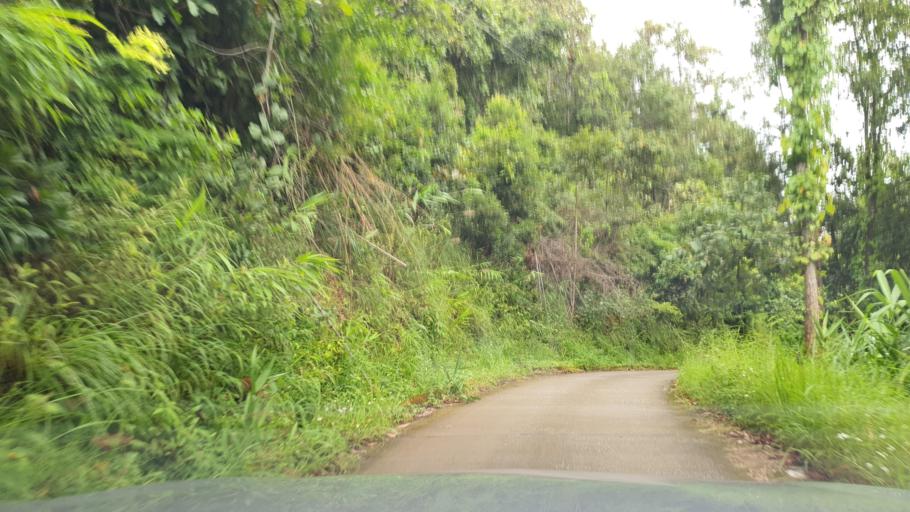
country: TH
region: Chiang Mai
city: Mae Taeng
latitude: 19.2333
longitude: 98.9308
